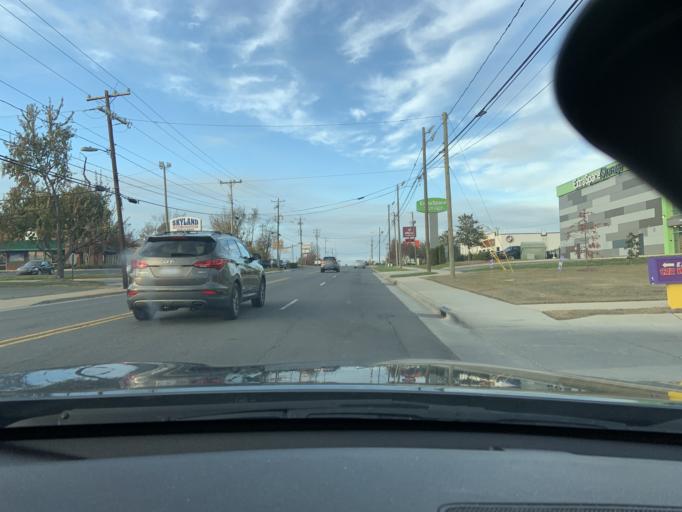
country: US
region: North Carolina
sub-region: Mecklenburg County
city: Charlotte
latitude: 35.1784
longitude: -80.8758
